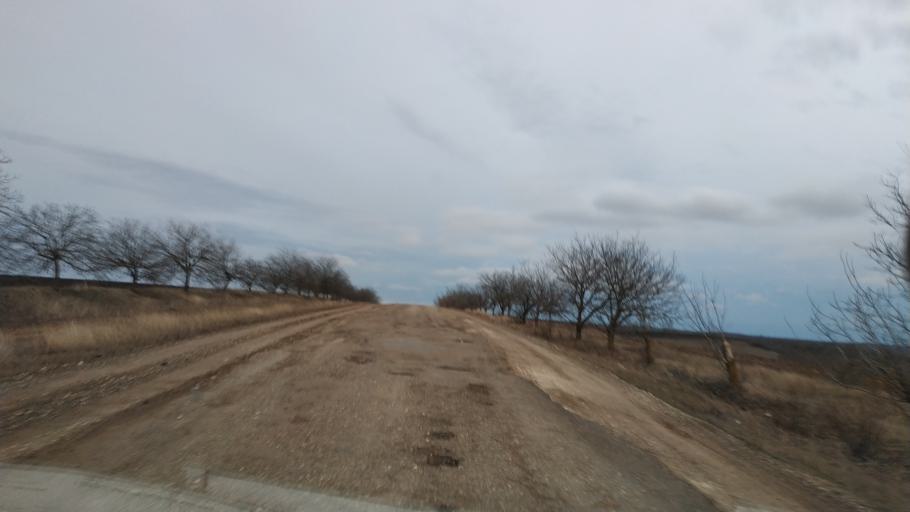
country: MD
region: Causeni
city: Causeni
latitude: 46.5751
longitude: 29.3895
